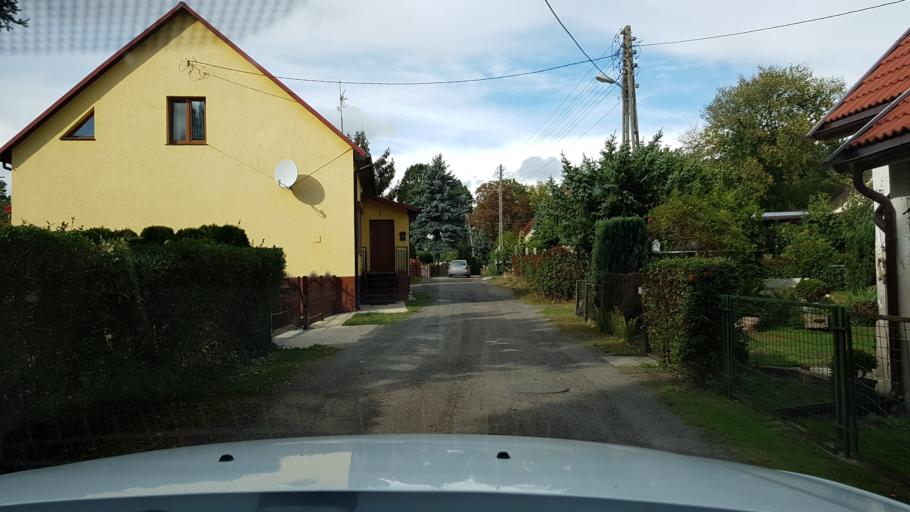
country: PL
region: West Pomeranian Voivodeship
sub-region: Powiat gryfinski
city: Gryfino
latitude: 53.3021
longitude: 14.5072
